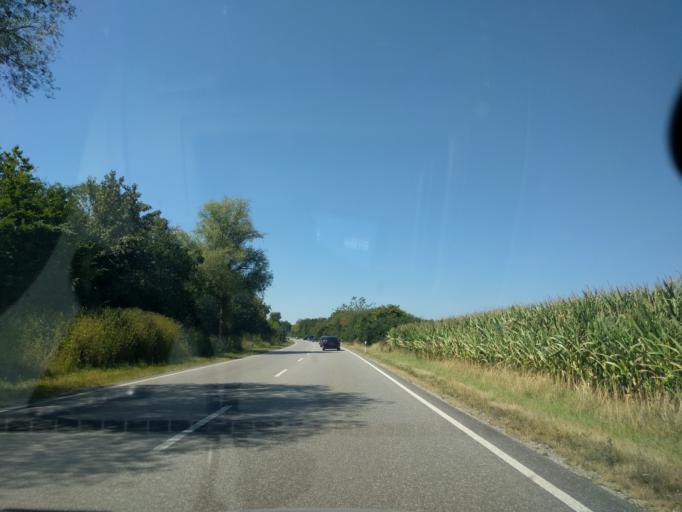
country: DE
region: Bavaria
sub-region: Upper Bavaria
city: Emmering
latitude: 48.1933
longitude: 11.2834
